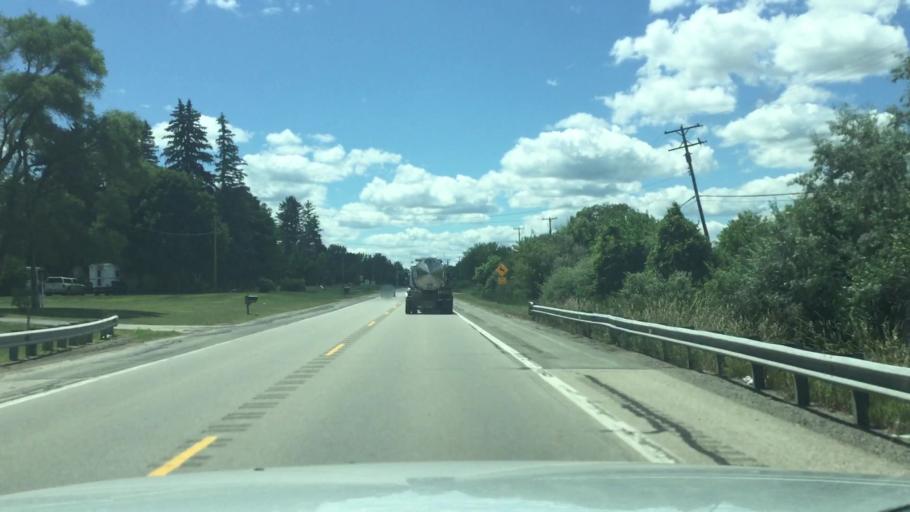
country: US
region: Michigan
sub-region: Saginaw County
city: Shields
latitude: 43.4075
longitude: -84.1309
